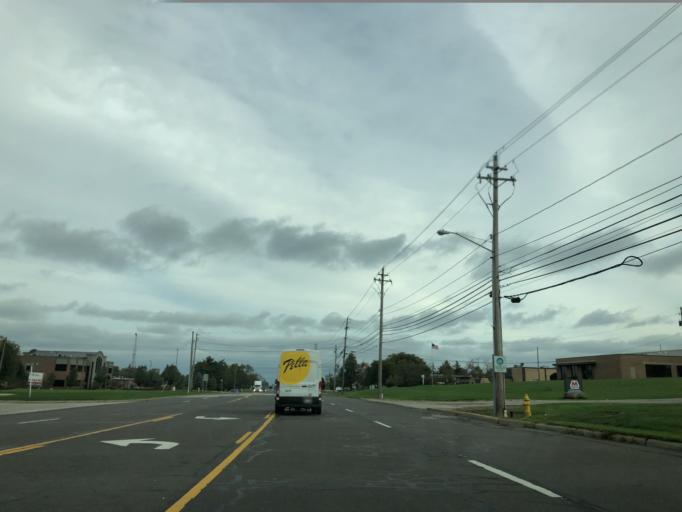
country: US
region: Ohio
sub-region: Summit County
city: Richfield
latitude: 41.2783
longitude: -81.6273
